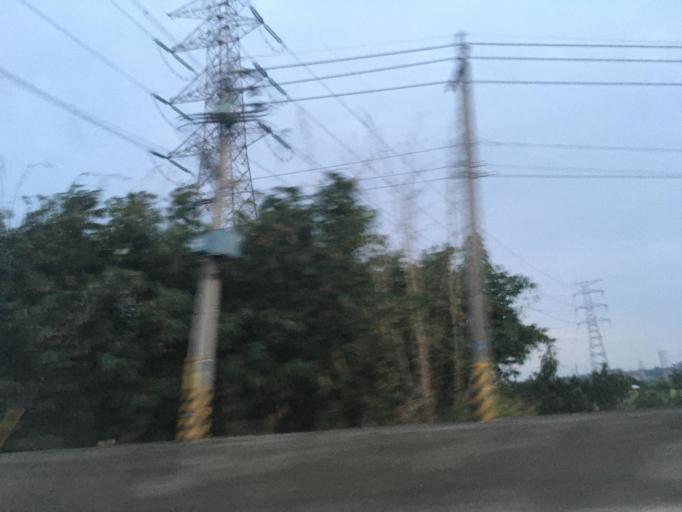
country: TW
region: Taiwan
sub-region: Chiayi
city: Jiayi Shi
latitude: 23.5768
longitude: 120.4589
